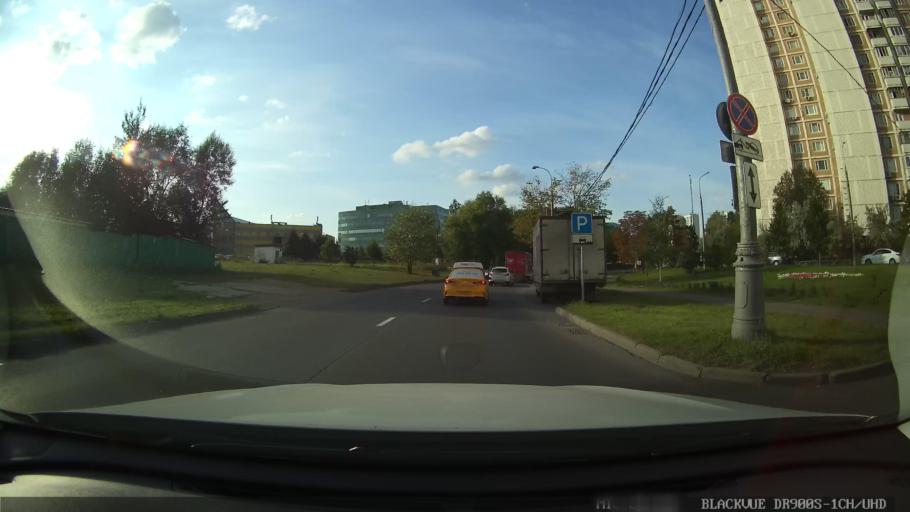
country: RU
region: Moskovskaya
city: Marfino
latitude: 55.7102
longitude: 37.3915
